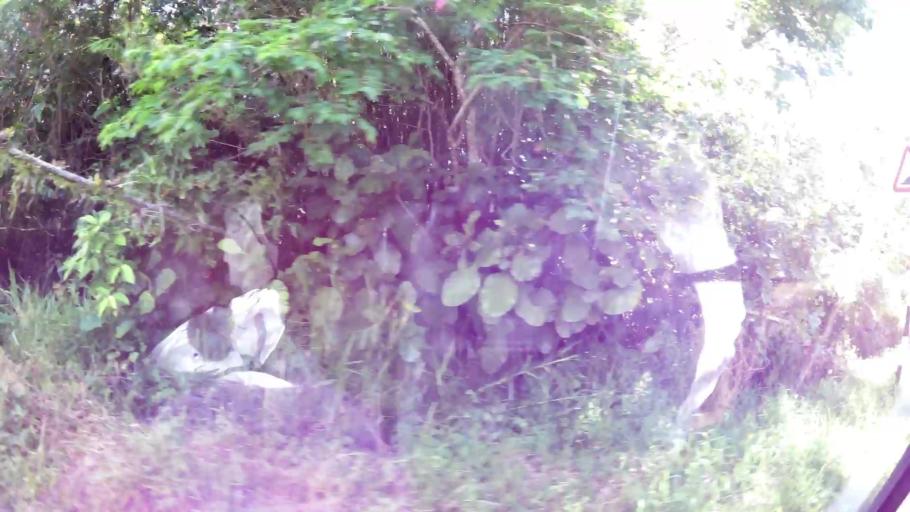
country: BN
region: Brunei and Muara
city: Bandar Seri Begawan
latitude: 5.0302
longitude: 115.0481
